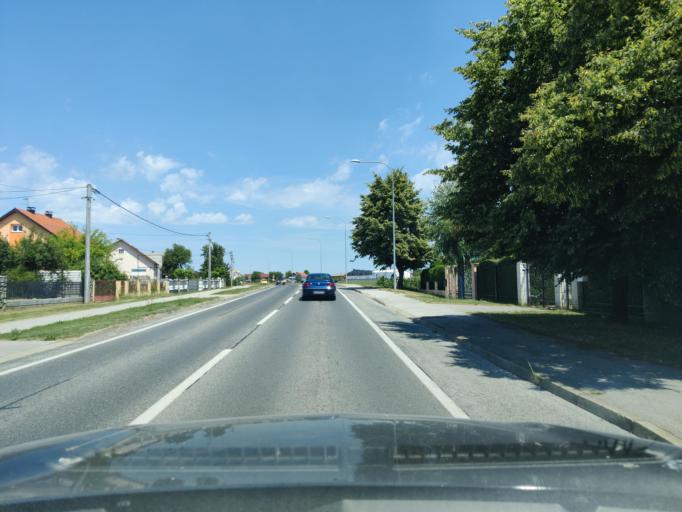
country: HR
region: Medimurska
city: Senkovec
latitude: 46.4098
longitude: 16.4225
